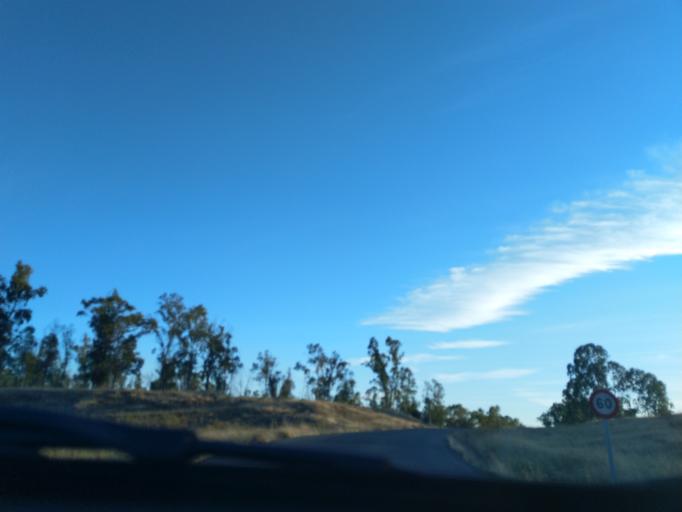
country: ES
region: Extremadura
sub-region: Provincia de Badajoz
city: Berlanga
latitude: 38.2726
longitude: -5.8210
